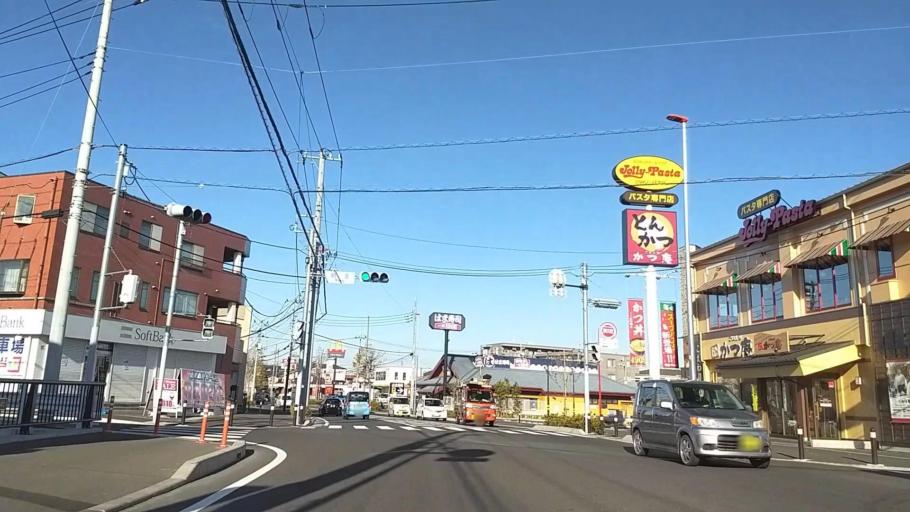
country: JP
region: Tokyo
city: Chofugaoka
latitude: 35.6212
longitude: 139.5515
